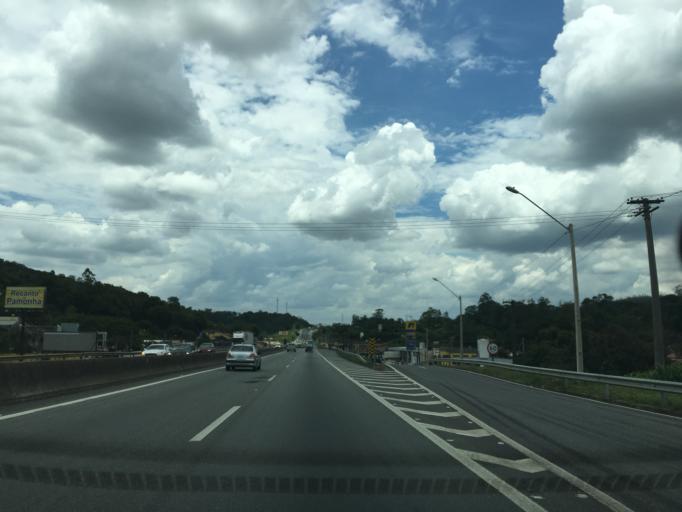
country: BR
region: Sao Paulo
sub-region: Mairipora
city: Mairipora
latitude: -23.2189
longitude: -46.5953
